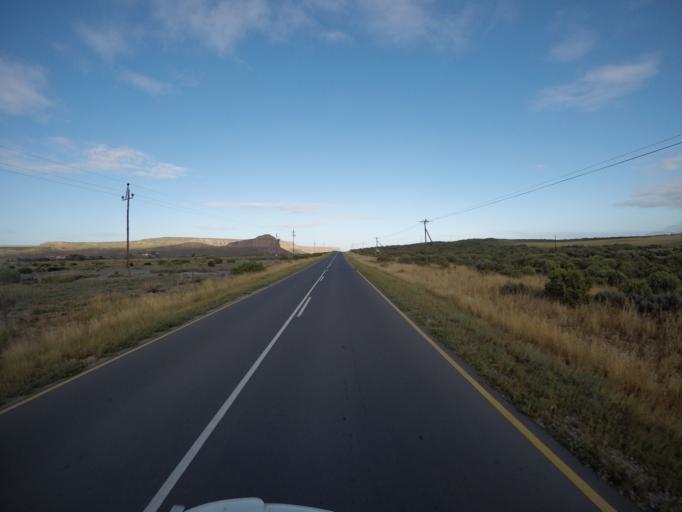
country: ZA
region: Western Cape
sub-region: West Coast District Municipality
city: Clanwilliam
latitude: -32.3123
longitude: 18.3708
